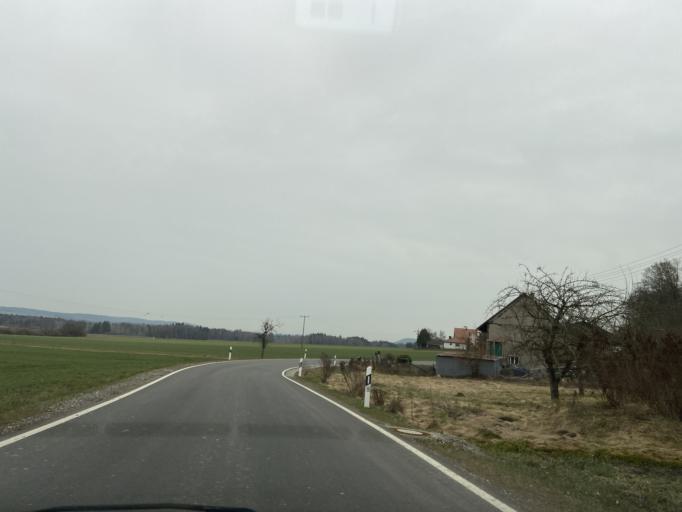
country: DE
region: Baden-Wuerttemberg
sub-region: Tuebingen Region
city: Illmensee
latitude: 47.9040
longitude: 9.3578
